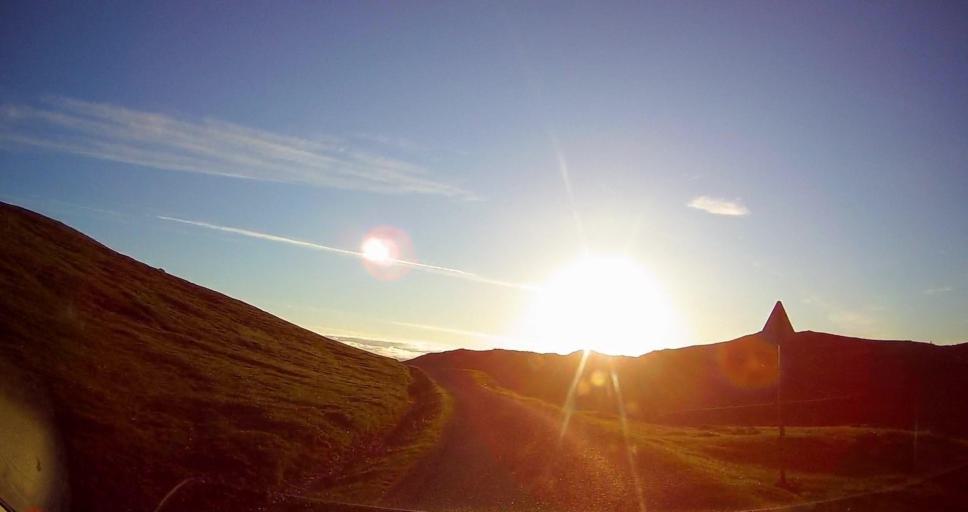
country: GB
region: Scotland
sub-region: Shetland Islands
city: Lerwick
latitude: 60.4485
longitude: -1.4168
